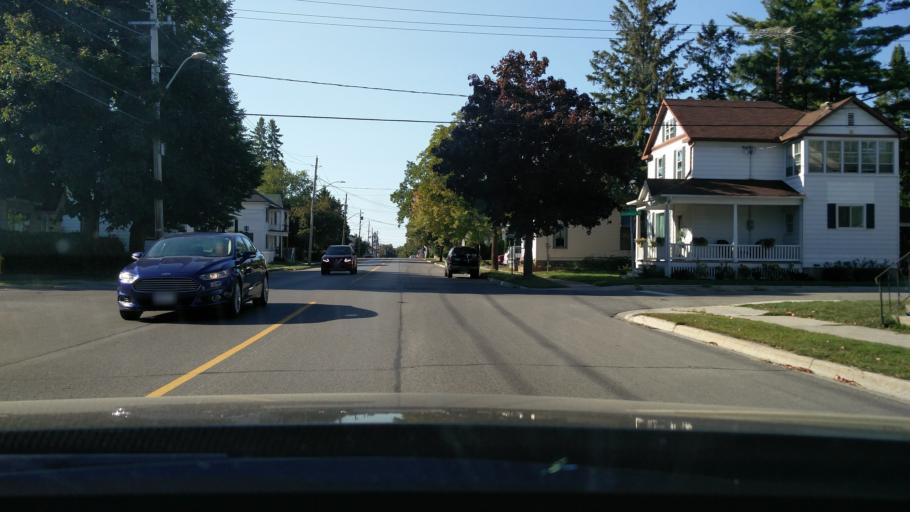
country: CA
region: Ontario
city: Perth
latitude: 44.8950
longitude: -76.2436
